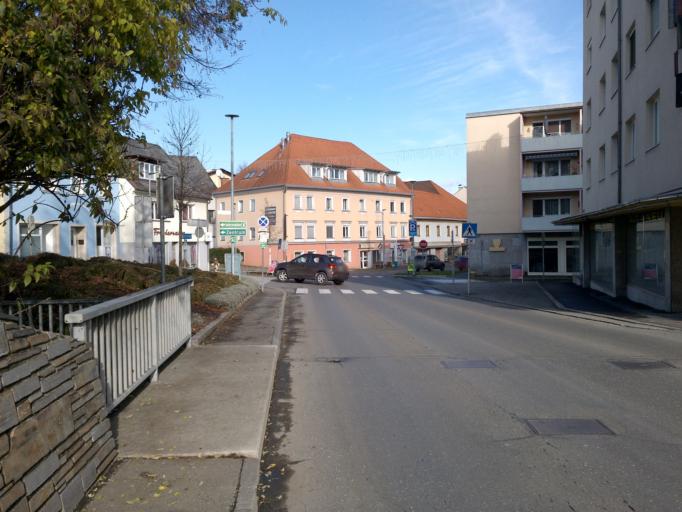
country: AT
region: Styria
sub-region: Politischer Bezirk Murtal
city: Knittelfeld
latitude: 47.2150
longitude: 14.8317
